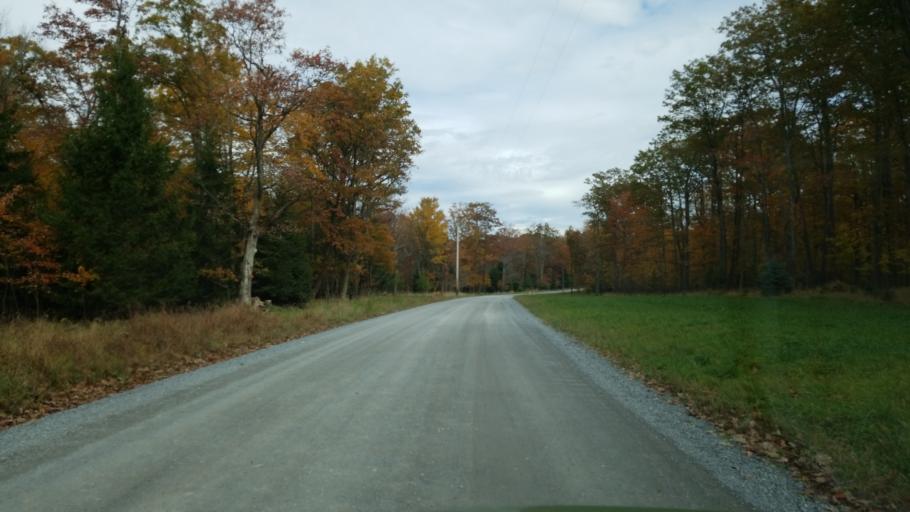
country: US
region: Pennsylvania
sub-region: Clearfield County
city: Clearfield
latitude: 41.1589
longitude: -78.4559
